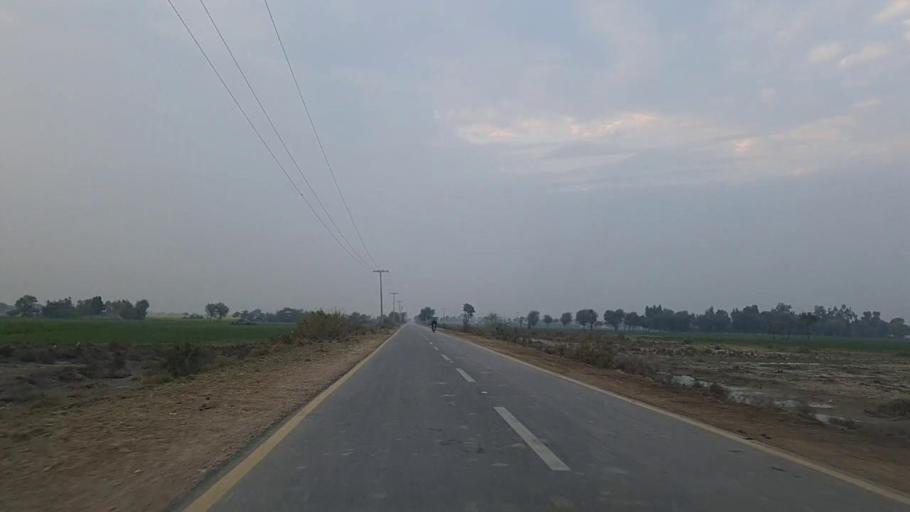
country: PK
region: Sindh
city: Jam Sahib
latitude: 26.3141
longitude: 68.5772
